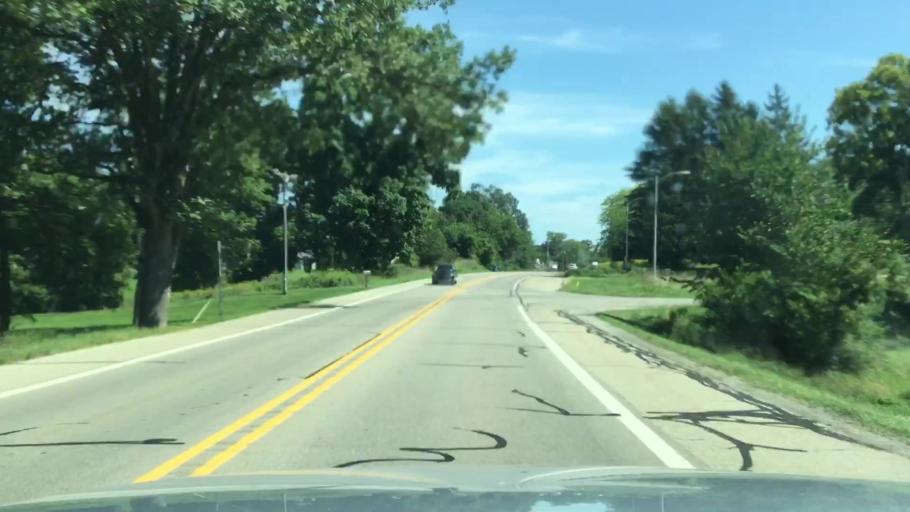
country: US
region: Michigan
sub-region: Washtenaw County
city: Manchester
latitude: 42.0651
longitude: -84.1076
